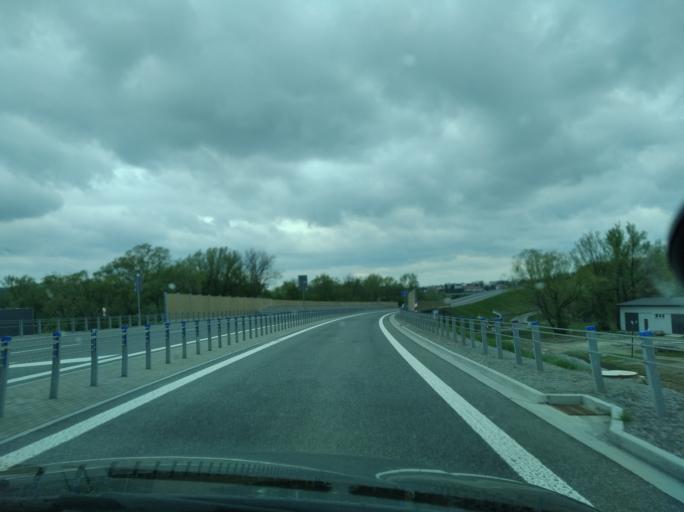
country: PL
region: Subcarpathian Voivodeship
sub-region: Powiat sanocki
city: Sanok
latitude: 49.5641
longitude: 22.1549
